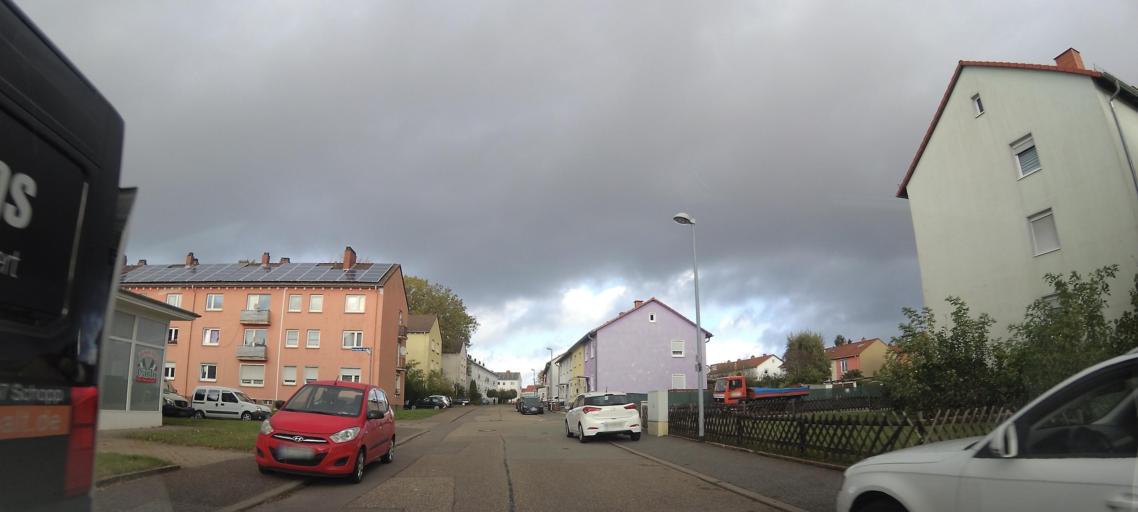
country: DE
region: Rheinland-Pfalz
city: Pirmasens
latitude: 49.1912
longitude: 7.5921
